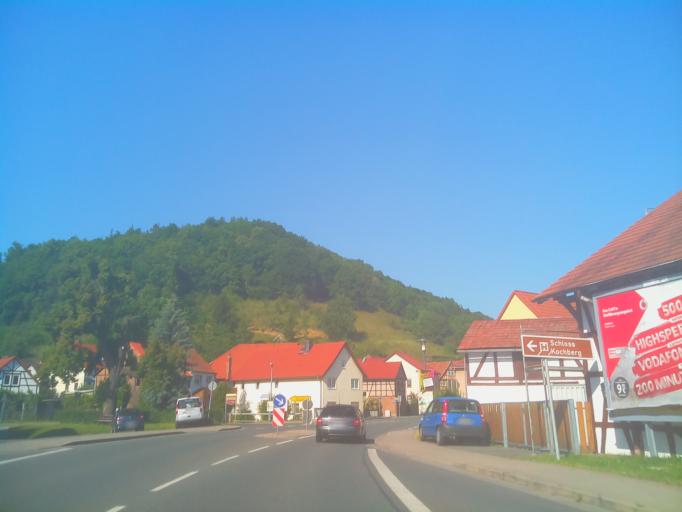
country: DE
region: Thuringia
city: Rudolstadt
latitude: 50.7303
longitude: 11.3914
